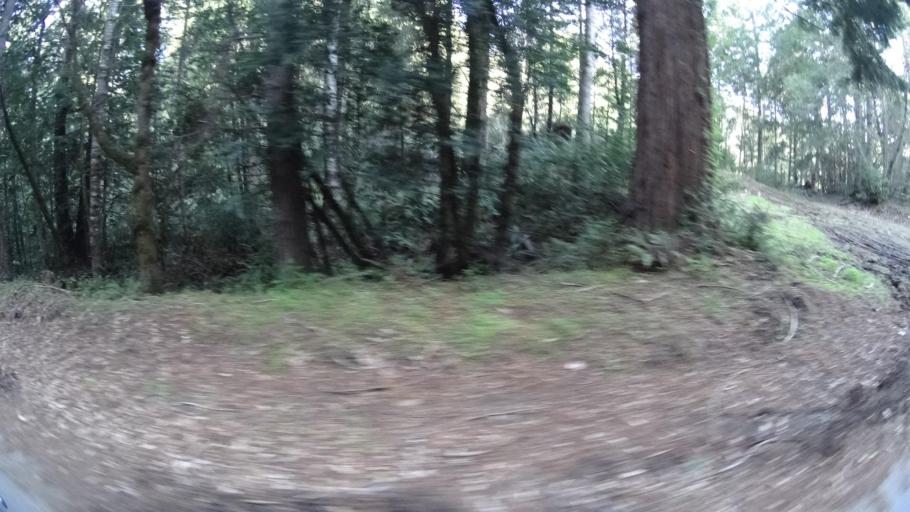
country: US
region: California
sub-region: Humboldt County
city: Blue Lake
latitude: 40.7041
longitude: -123.9381
